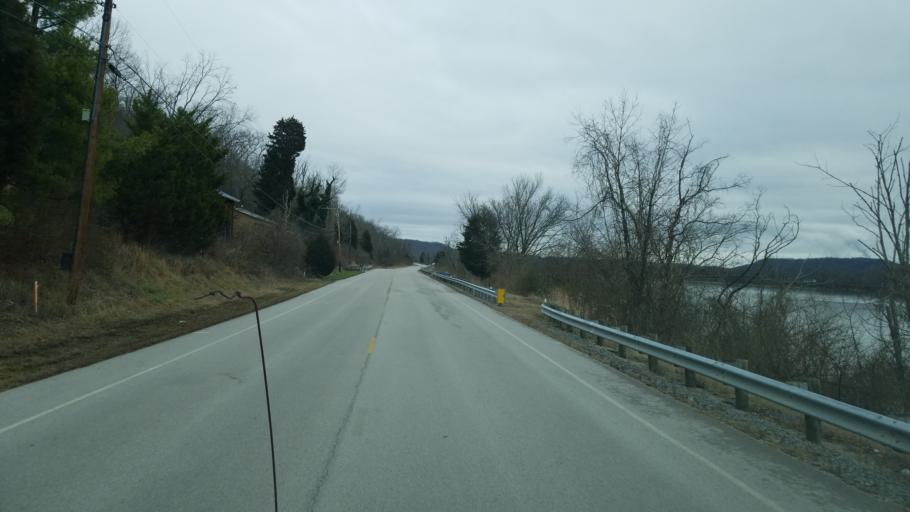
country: US
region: Ohio
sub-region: Brown County
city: Ripley
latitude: 38.7690
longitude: -83.9035
